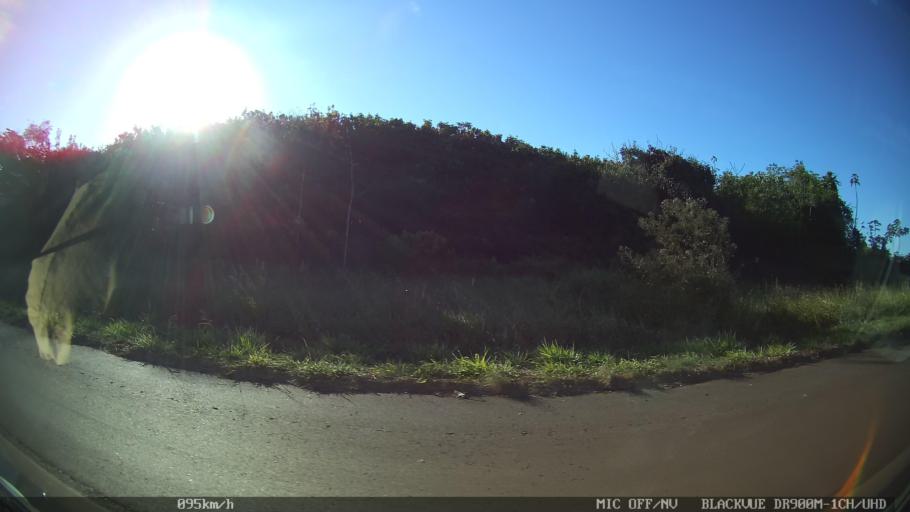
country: BR
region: Sao Paulo
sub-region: Guapiacu
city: Guapiacu
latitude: -20.7692
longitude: -49.2102
